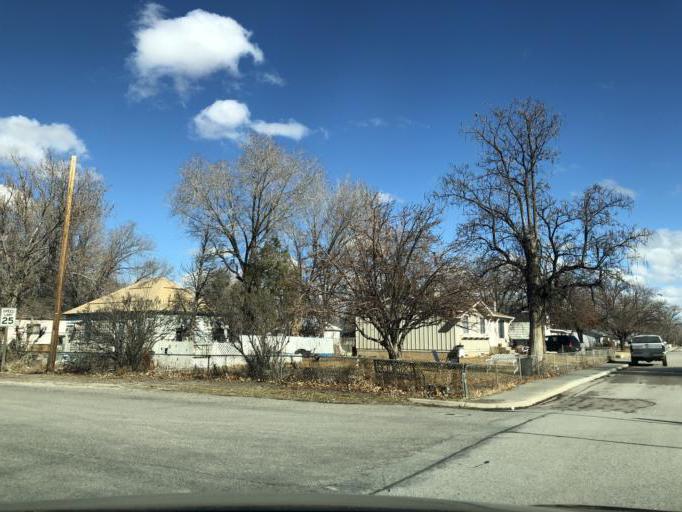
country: US
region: Utah
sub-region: Carbon County
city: East Carbon City
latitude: 38.9906
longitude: -110.1610
